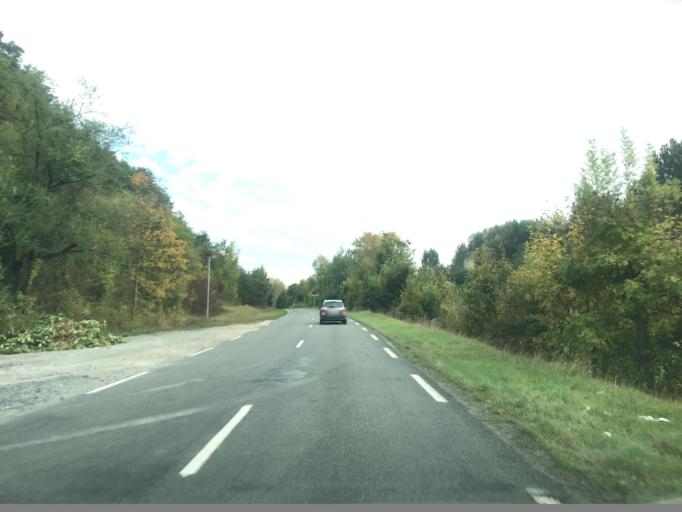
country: FR
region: Haute-Normandie
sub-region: Departement de l'Eure
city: Heudreville-sur-Eure
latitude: 49.1438
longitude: 1.1982
